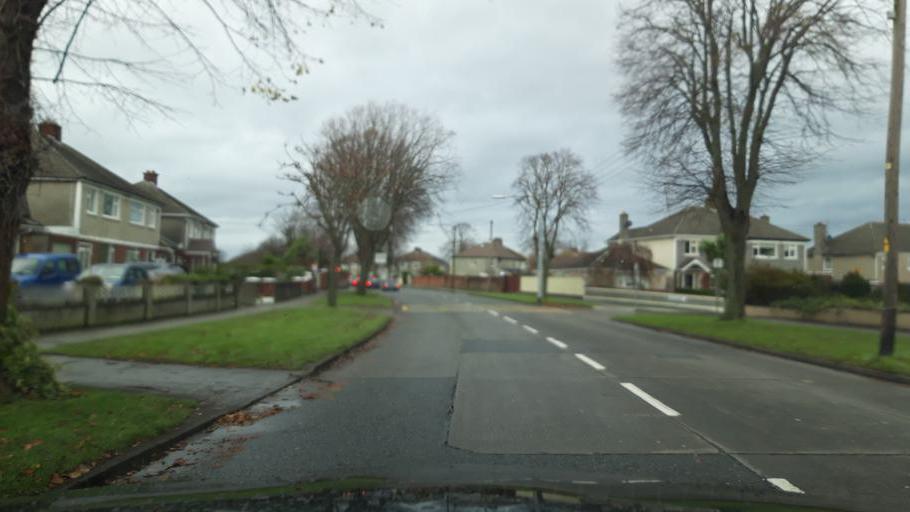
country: IE
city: Killester
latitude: 53.3761
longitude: -6.1951
